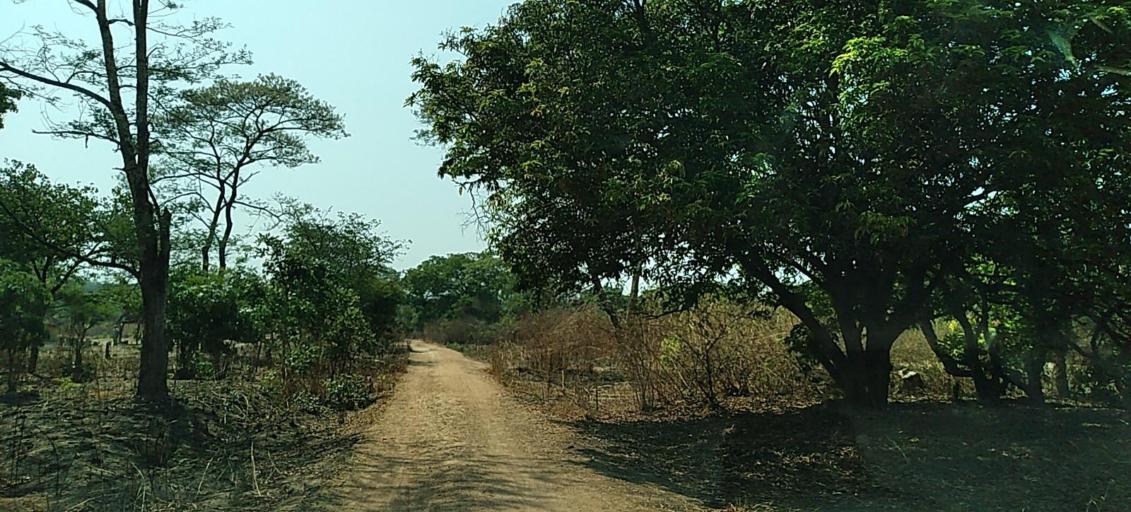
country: ZM
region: Copperbelt
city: Luanshya
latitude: -13.2797
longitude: 28.3111
